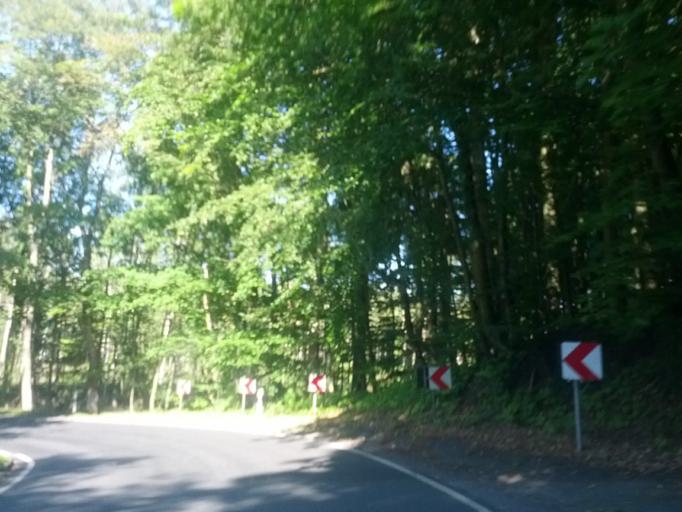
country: DE
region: Mecklenburg-Vorpommern
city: Ostseebad Gohren
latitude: 54.3428
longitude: 13.7093
